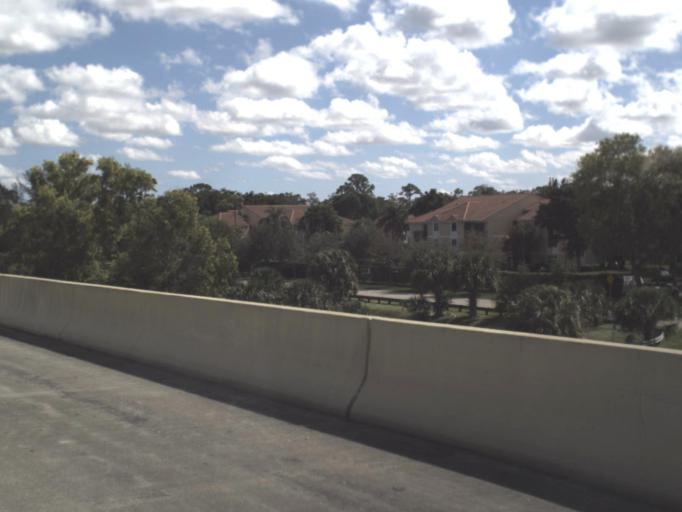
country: US
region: Florida
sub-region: Broward County
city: Parkland
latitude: 26.3015
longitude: -80.2368
